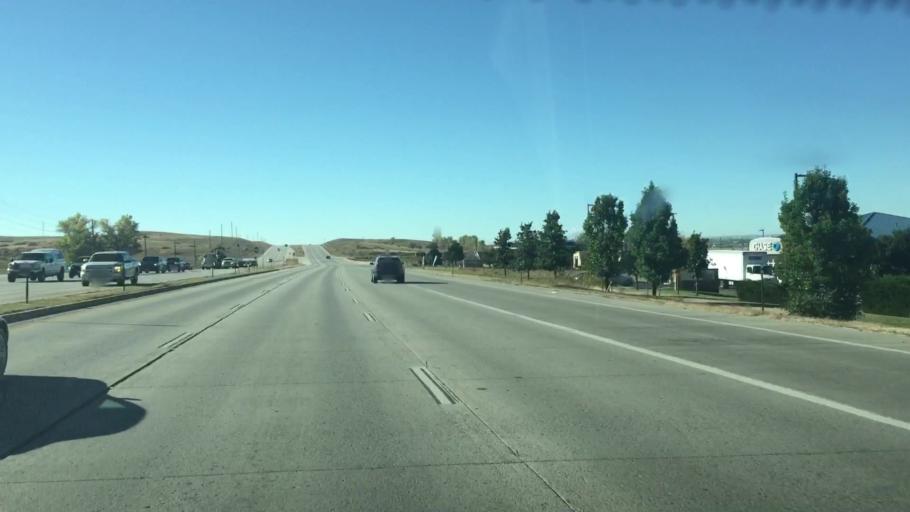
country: US
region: Colorado
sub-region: Douglas County
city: The Pinery
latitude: 39.4780
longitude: -104.7582
